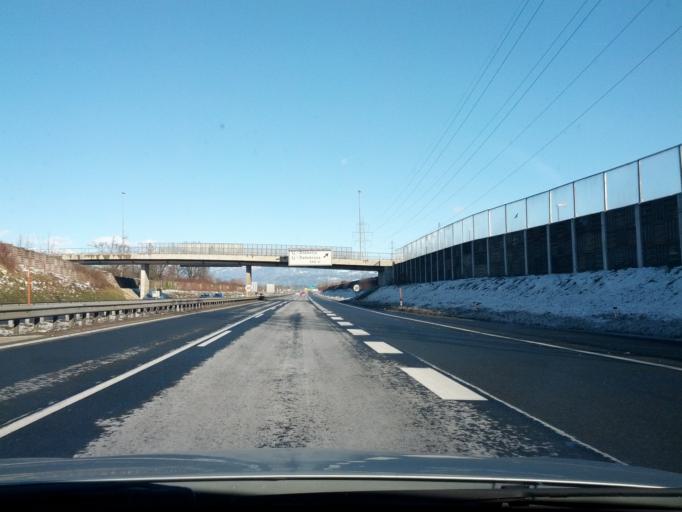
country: SI
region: Dol pri Ljubljani
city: Dol pri Ljubljani
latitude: 46.0739
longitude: 14.5794
